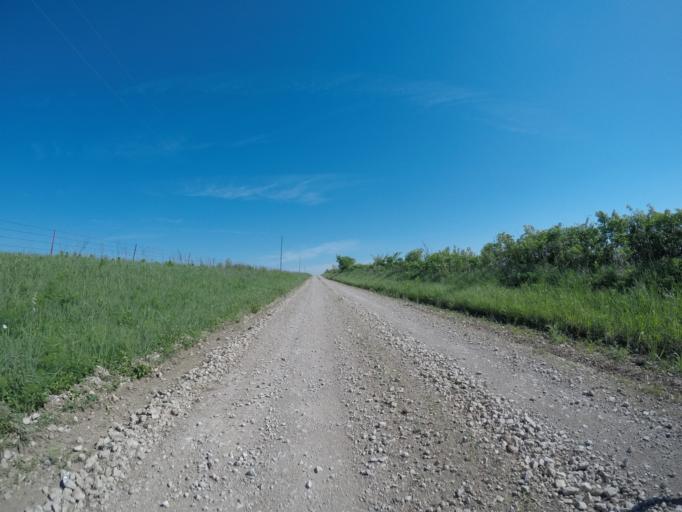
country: US
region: Kansas
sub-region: Wabaunsee County
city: Alma
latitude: 38.9514
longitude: -96.1138
